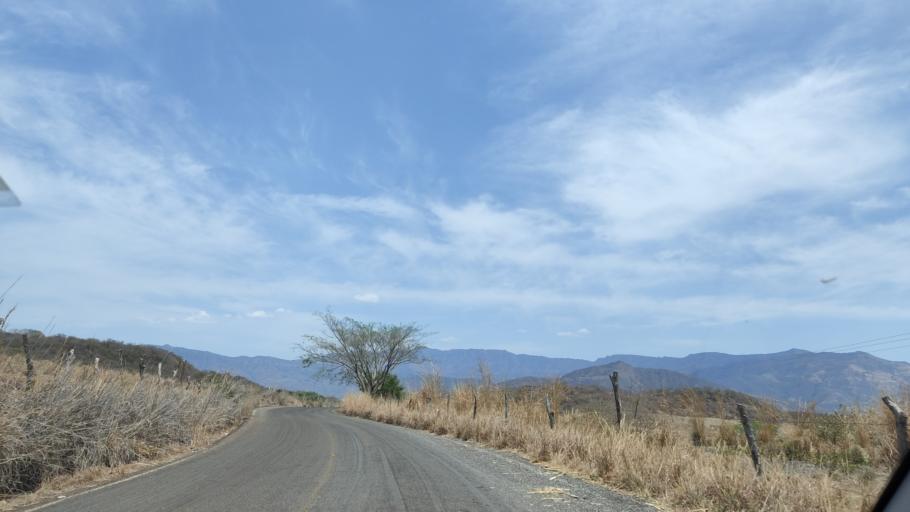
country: MX
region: Nayarit
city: Santa Maria del Oro
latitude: 21.5069
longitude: -104.6014
